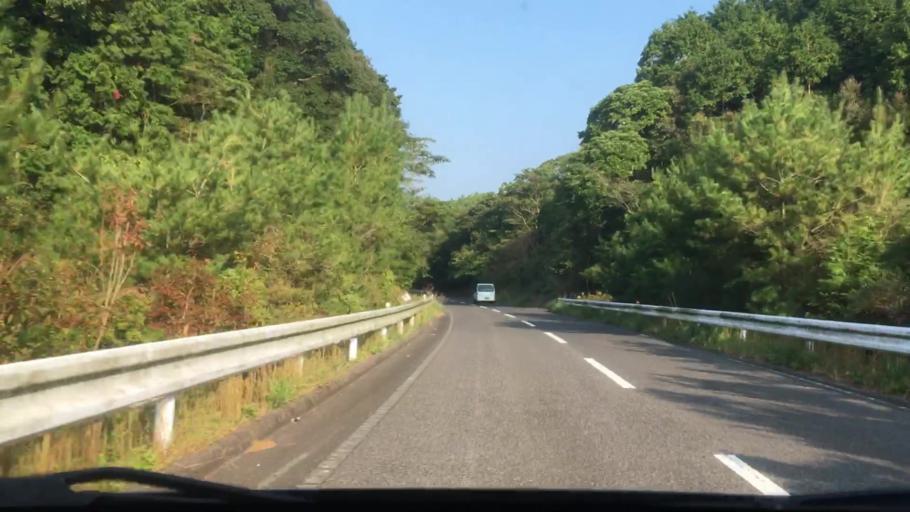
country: JP
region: Nagasaki
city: Sasebo
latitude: 33.0246
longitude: 129.6975
